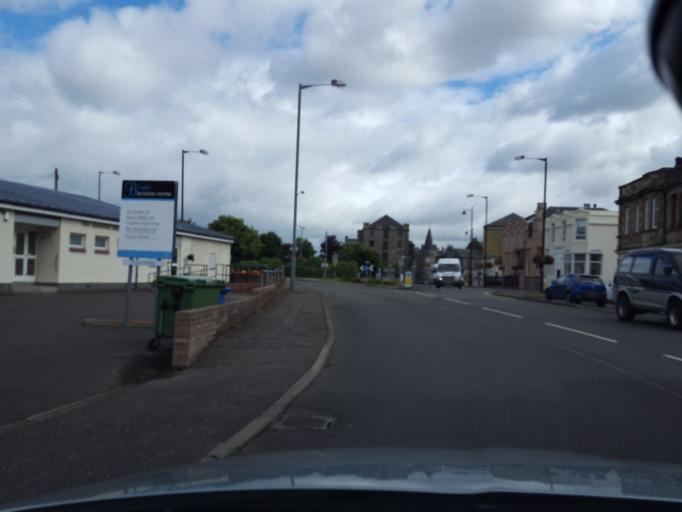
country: GB
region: Scotland
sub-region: Falkirk
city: Bo'ness
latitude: 56.0160
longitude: -3.6114
